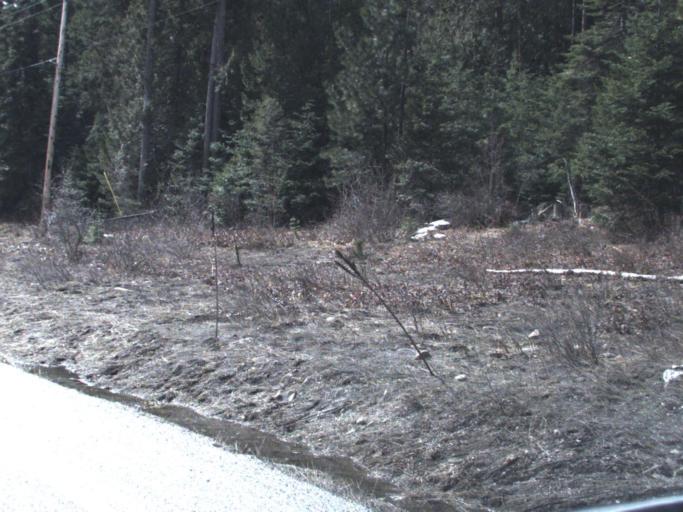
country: US
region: Washington
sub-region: Pend Oreille County
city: Newport
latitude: 48.4545
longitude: -117.3267
